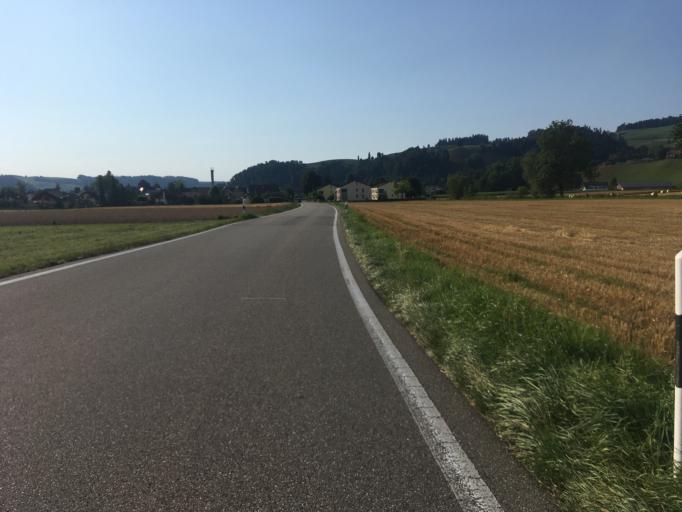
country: CH
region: Bern
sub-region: Emmental District
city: Lutzelfluh
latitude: 47.0129
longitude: 7.6698
